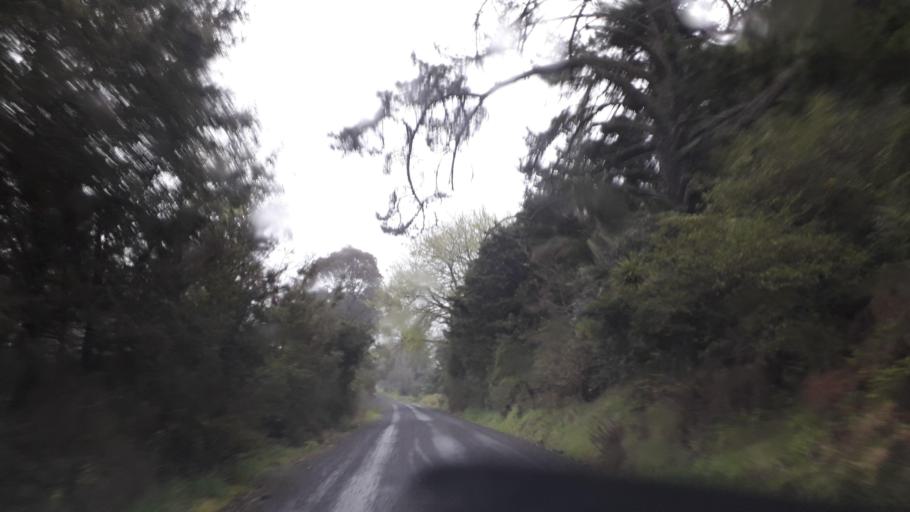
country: NZ
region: Northland
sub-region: Far North District
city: Waimate North
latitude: -35.4906
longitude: 173.7003
